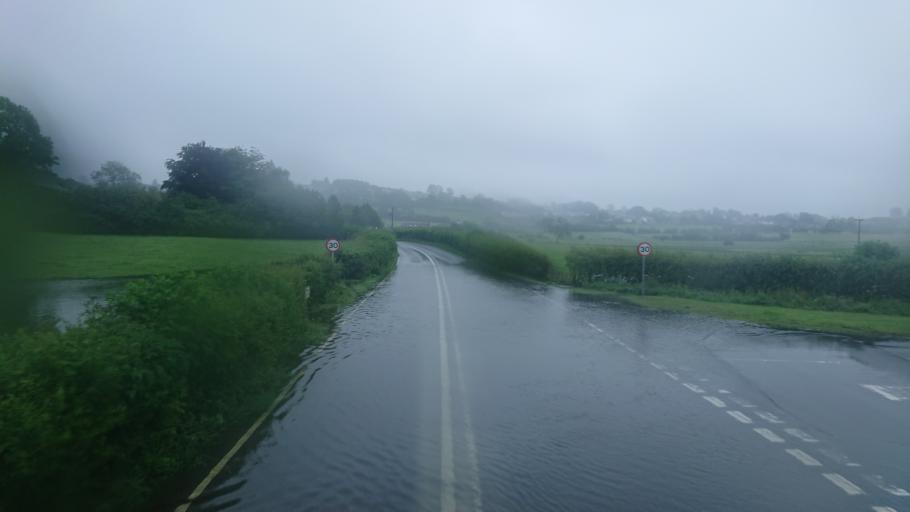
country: GB
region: England
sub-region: Cumbria
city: Milnthorpe
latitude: 54.1928
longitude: -2.7223
